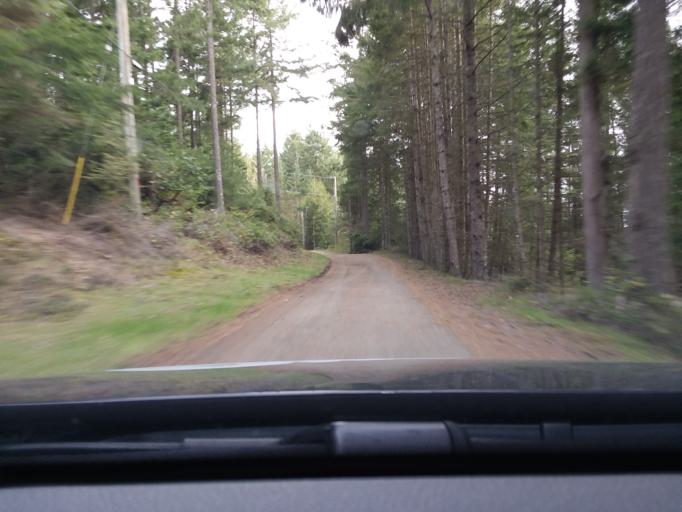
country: CA
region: British Columbia
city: North Saanich
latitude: 48.8763
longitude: -123.3301
